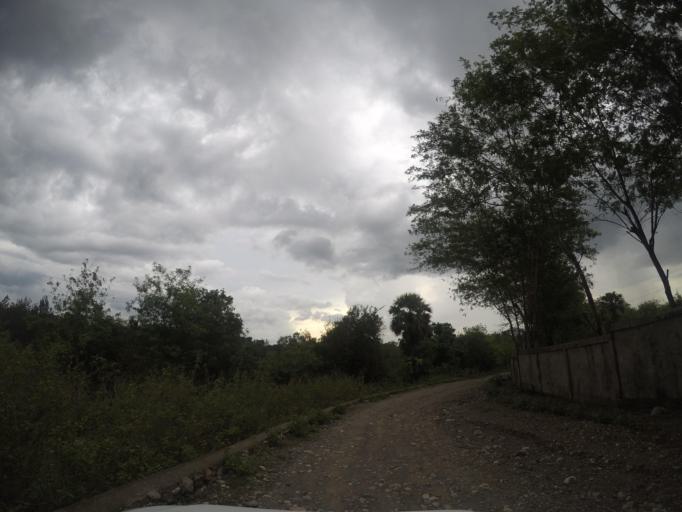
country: TL
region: Bobonaro
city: Maliana
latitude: -8.9752
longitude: 125.2244
